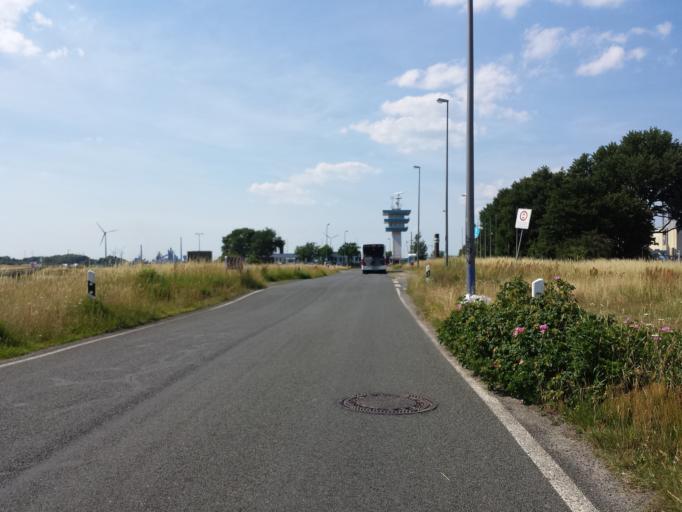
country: DE
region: Bremen
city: Bremen
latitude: 53.1073
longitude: 8.7419
